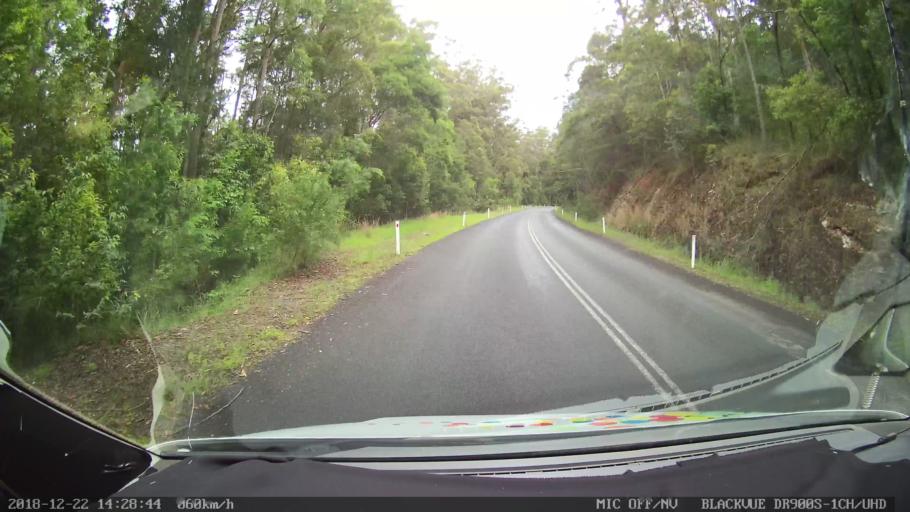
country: AU
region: New South Wales
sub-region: Bellingen
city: Dorrigo
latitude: -30.0752
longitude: 152.6370
